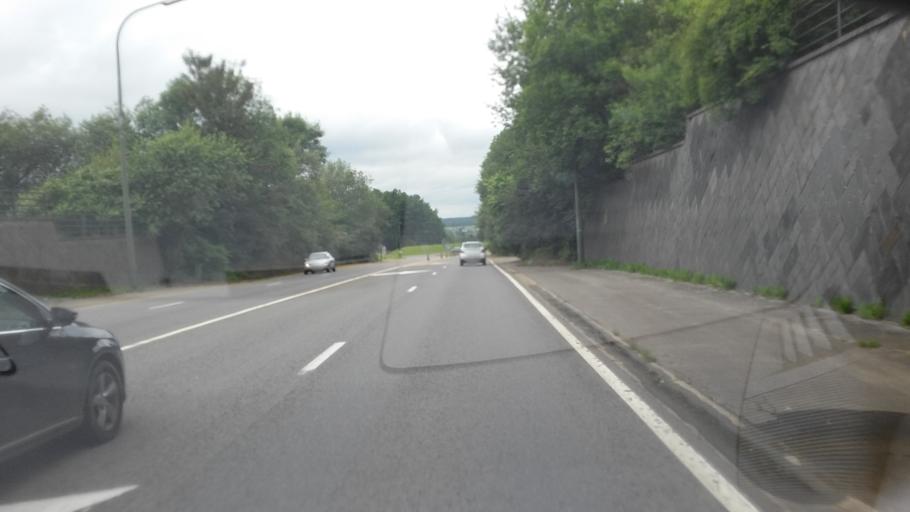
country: BE
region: Wallonia
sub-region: Province du Luxembourg
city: Arlon
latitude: 49.6872
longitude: 5.8215
